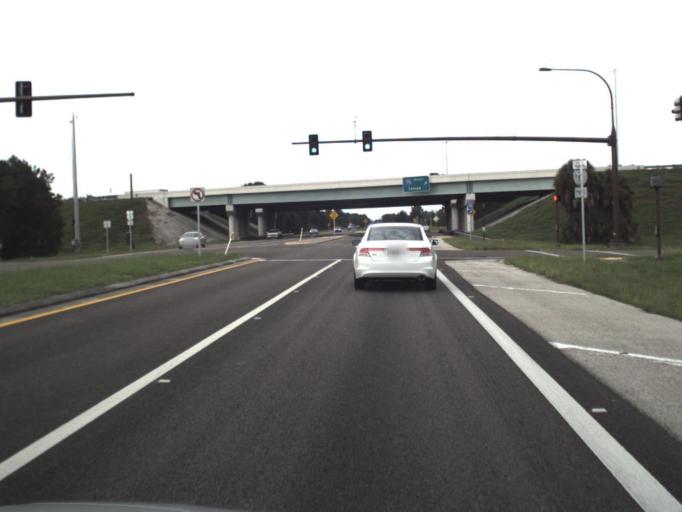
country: US
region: Florida
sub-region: Sarasota County
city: Plantation
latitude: 27.1097
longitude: -82.3843
